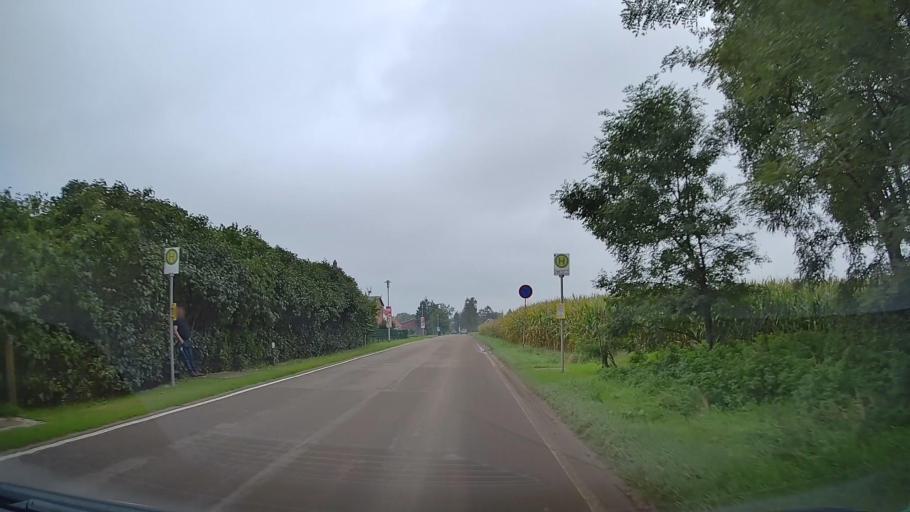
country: DE
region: Mecklenburg-Vorpommern
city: Blowatz
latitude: 53.9746
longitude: 11.5521
